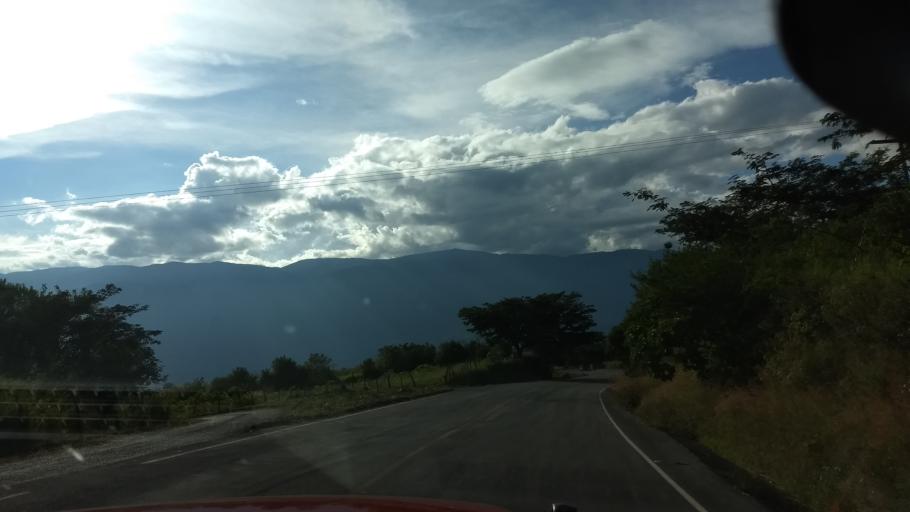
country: MX
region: Colima
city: Suchitlan
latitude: 19.4646
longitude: -103.7758
